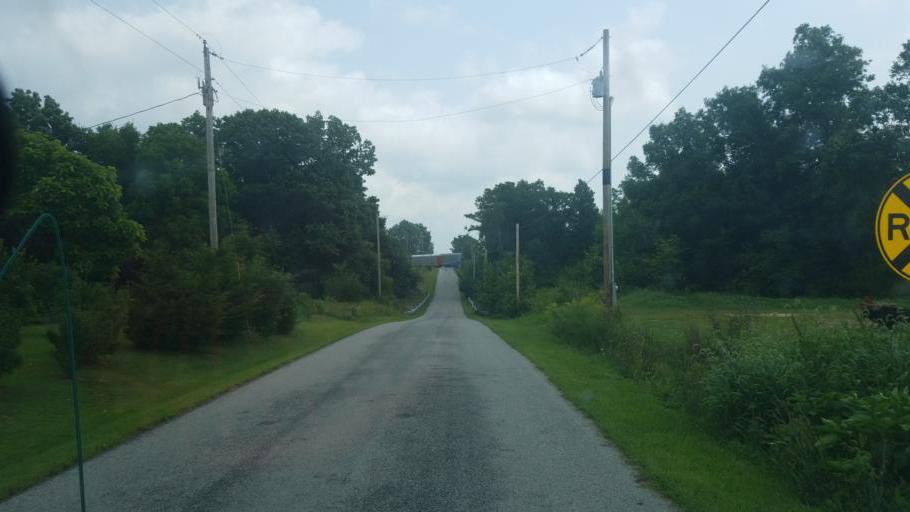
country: US
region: Ohio
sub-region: Huron County
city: Greenwich
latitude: 41.0615
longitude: -82.4619
